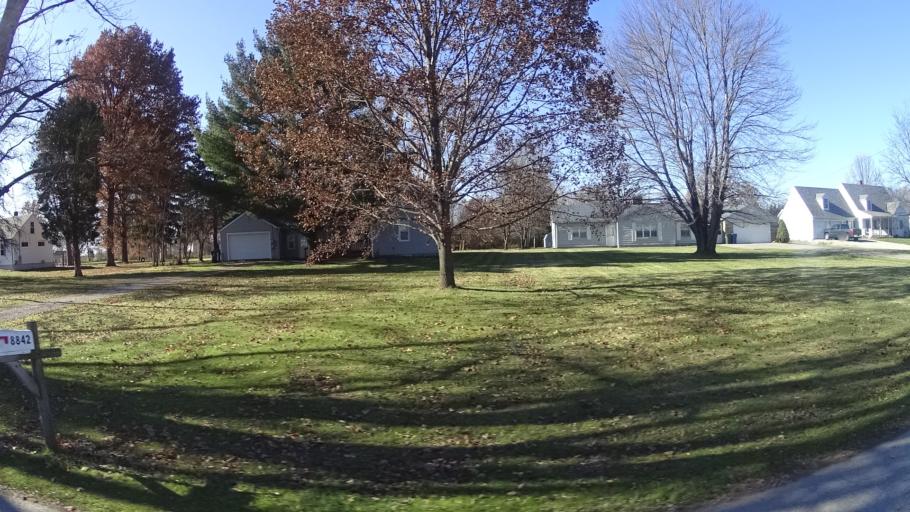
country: US
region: Ohio
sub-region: Lorain County
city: Elyria
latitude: 41.3629
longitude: -82.1586
